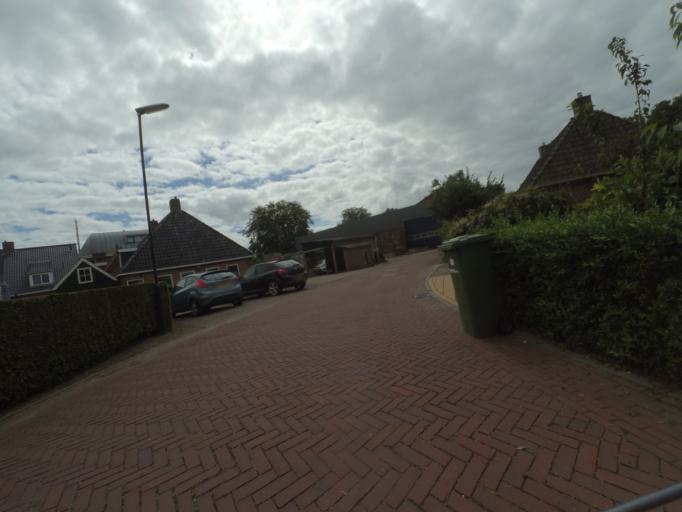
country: NL
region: Friesland
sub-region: Gemeente Kollumerland en Nieuwkruisland
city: Kollum
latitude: 53.3186
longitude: 6.1569
